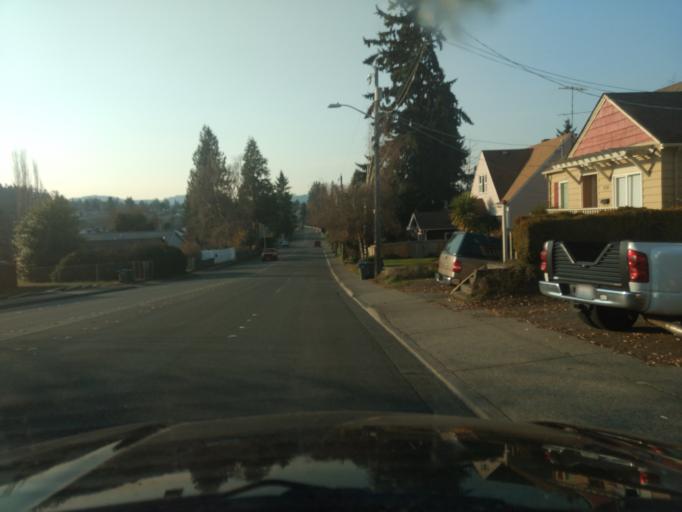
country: US
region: Washington
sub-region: Kitsap County
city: Bremerton
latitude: 47.5711
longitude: -122.6471
